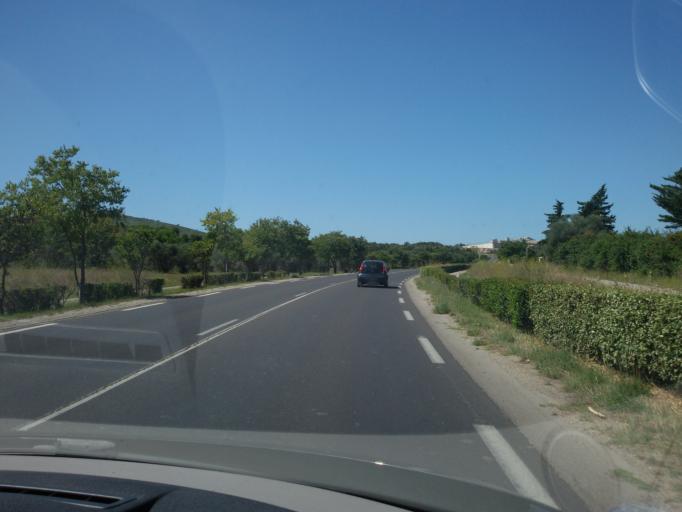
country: FR
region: Languedoc-Roussillon
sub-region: Departement de l'Herault
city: Villeneuve-les-Maguelone
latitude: 43.5437
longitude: 3.8380
